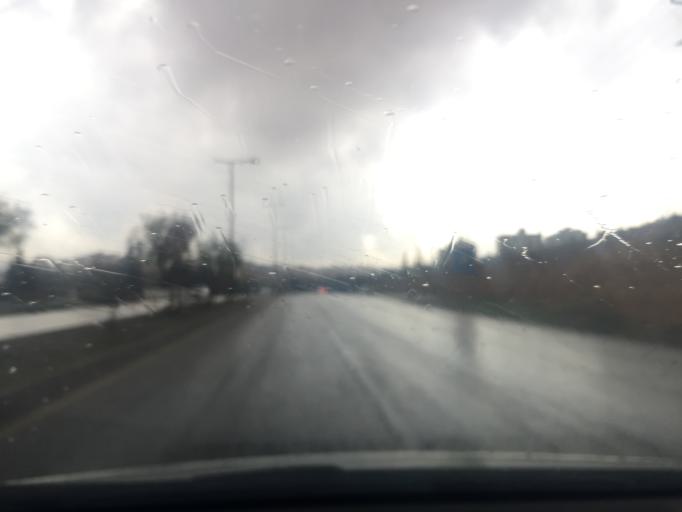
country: JO
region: Amman
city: Amman
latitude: 32.0216
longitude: 35.9412
